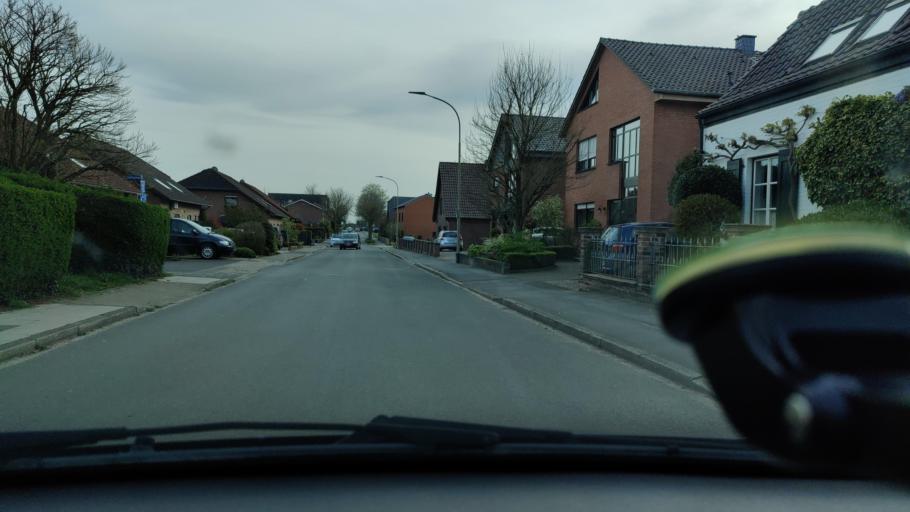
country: DE
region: North Rhine-Westphalia
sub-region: Regierungsbezirk Dusseldorf
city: Goch
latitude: 51.7051
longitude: 6.1624
